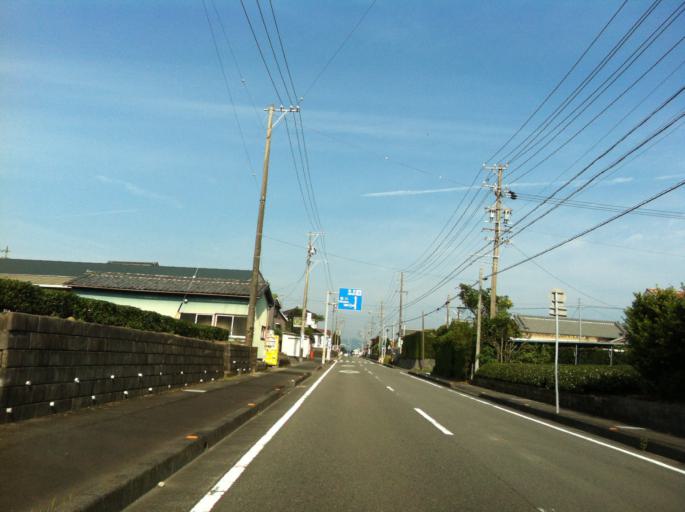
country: JP
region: Shizuoka
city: Kanaya
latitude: 34.7819
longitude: 138.1430
